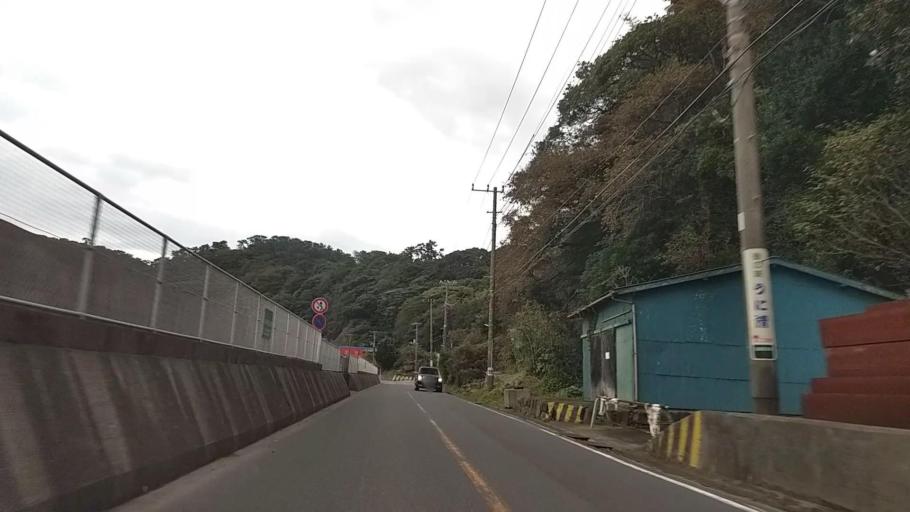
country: JP
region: Kanagawa
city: Yugawara
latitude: 35.1488
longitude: 139.1487
